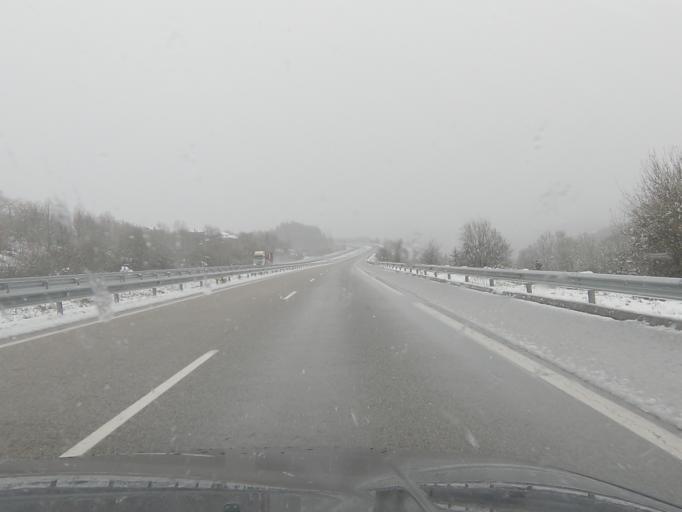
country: ES
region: Galicia
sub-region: Provincia de Ourense
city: Rios
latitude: 41.9904
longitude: -7.2591
